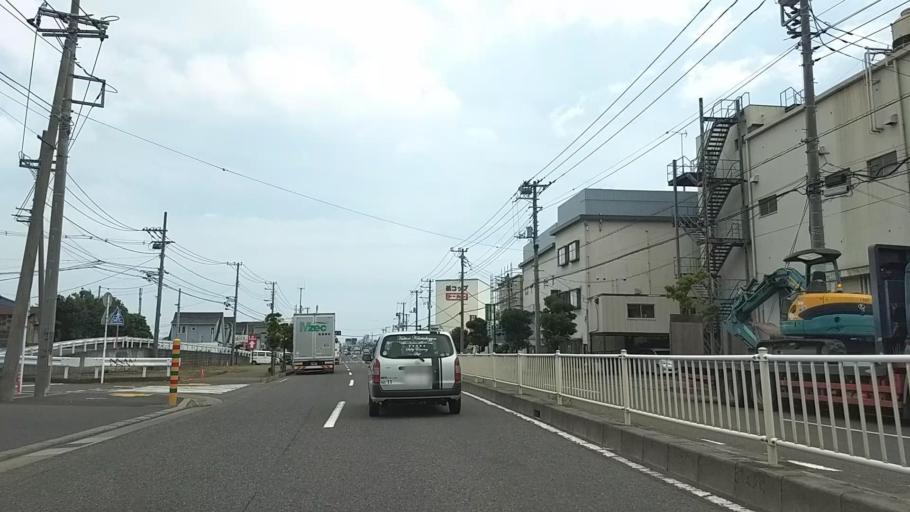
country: JP
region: Kanagawa
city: Minami-rinkan
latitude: 35.4518
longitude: 139.4184
